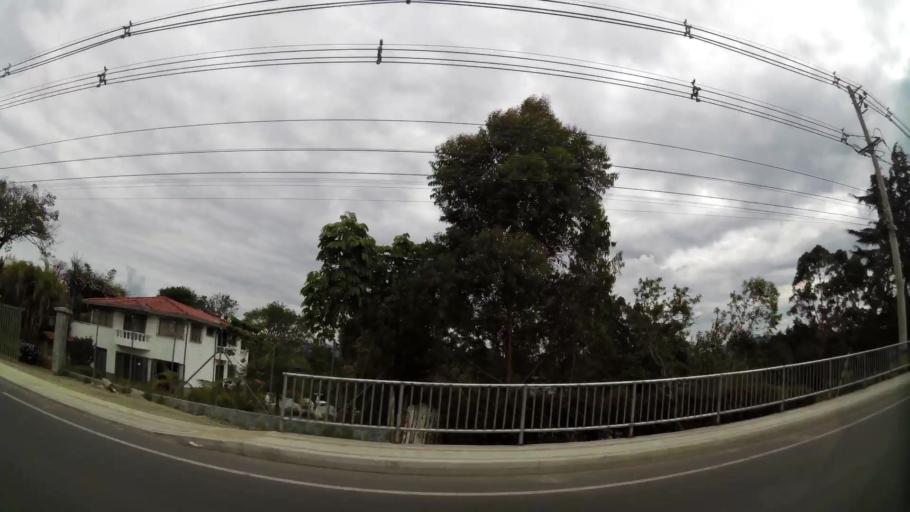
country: CO
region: Antioquia
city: Rionegro
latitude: 6.1478
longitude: -75.4215
